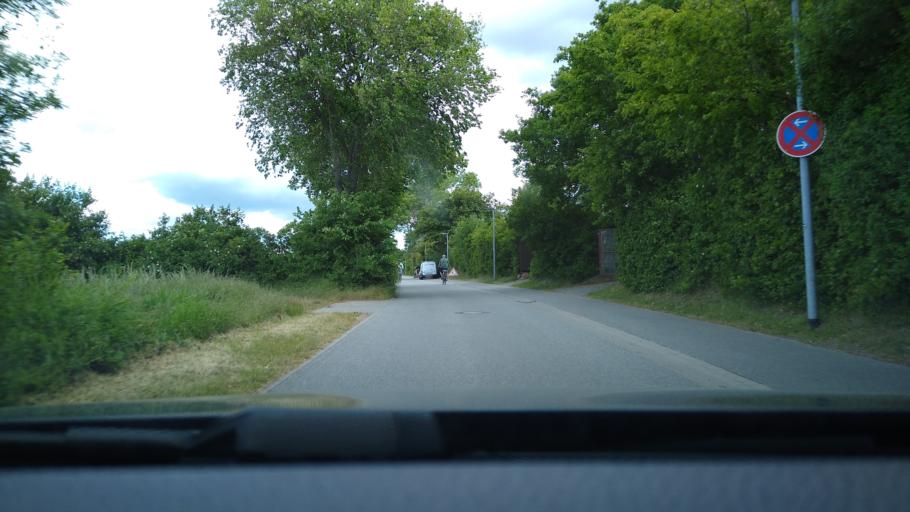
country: DE
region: Schleswig-Holstein
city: Dahme
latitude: 54.2106
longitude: 11.0897
